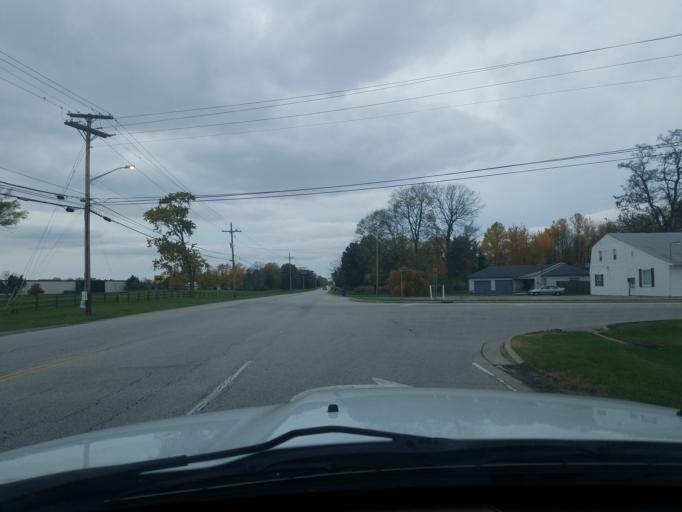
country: US
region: Indiana
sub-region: Shelby County
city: Shelbyville
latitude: 39.5471
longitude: -85.7874
